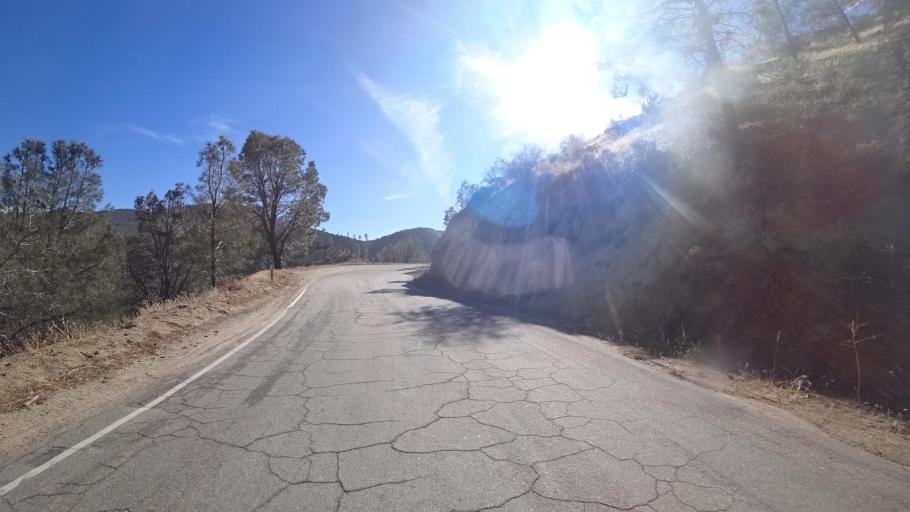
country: US
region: California
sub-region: Kern County
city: Bodfish
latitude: 35.5793
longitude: -118.5049
